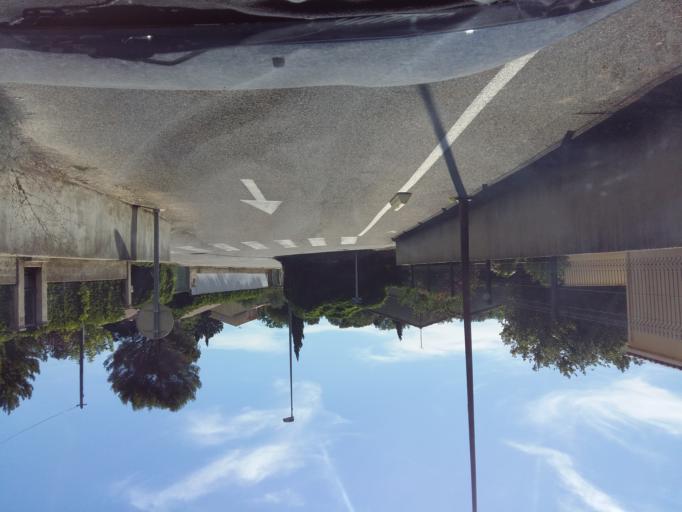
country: FR
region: Provence-Alpes-Cote d'Azur
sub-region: Departement du Vaucluse
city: Piolenc
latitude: 44.1820
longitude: 4.7610
